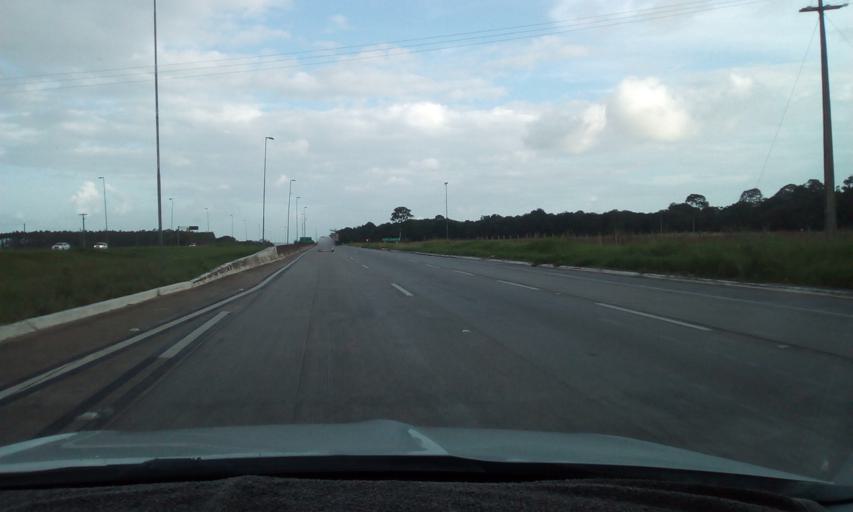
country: BR
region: Paraiba
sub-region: Cruz Do Espirito Santo
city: Cruz do Espirito Santo
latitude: -6.9907
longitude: -35.0711
